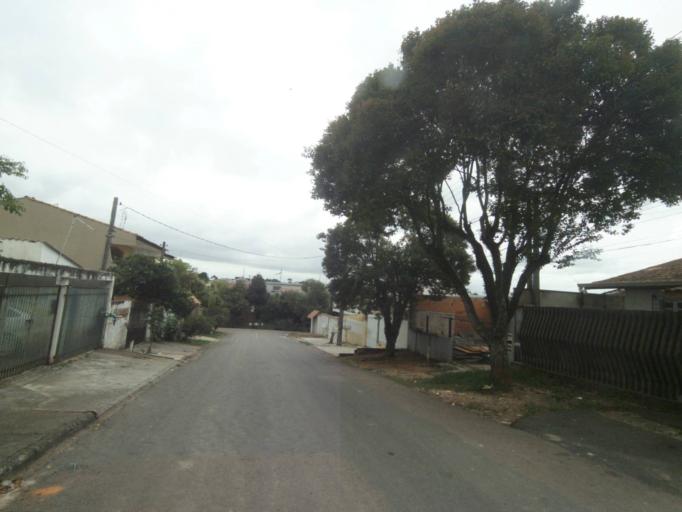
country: BR
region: Parana
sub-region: Sao Jose Dos Pinhais
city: Sao Jose dos Pinhais
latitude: -25.5456
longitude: -49.2750
